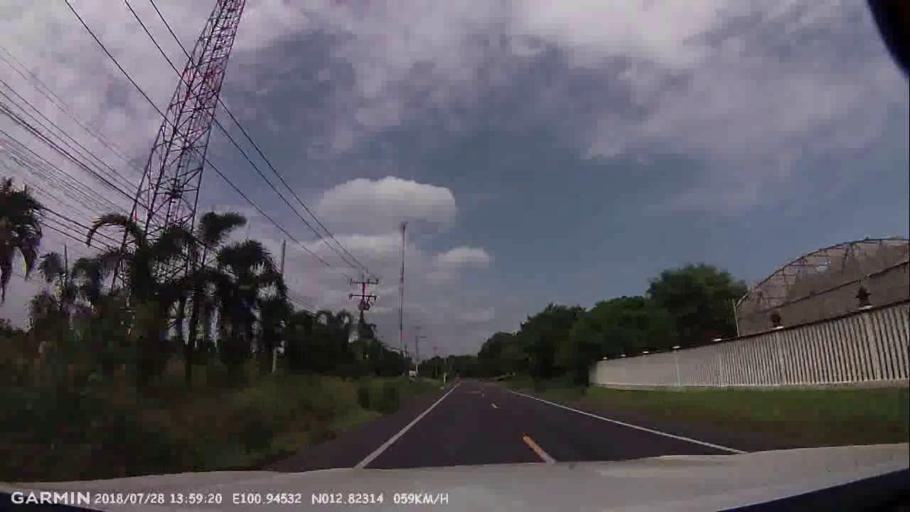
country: TH
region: Chon Buri
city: Phatthaya
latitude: 12.8231
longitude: 100.9455
